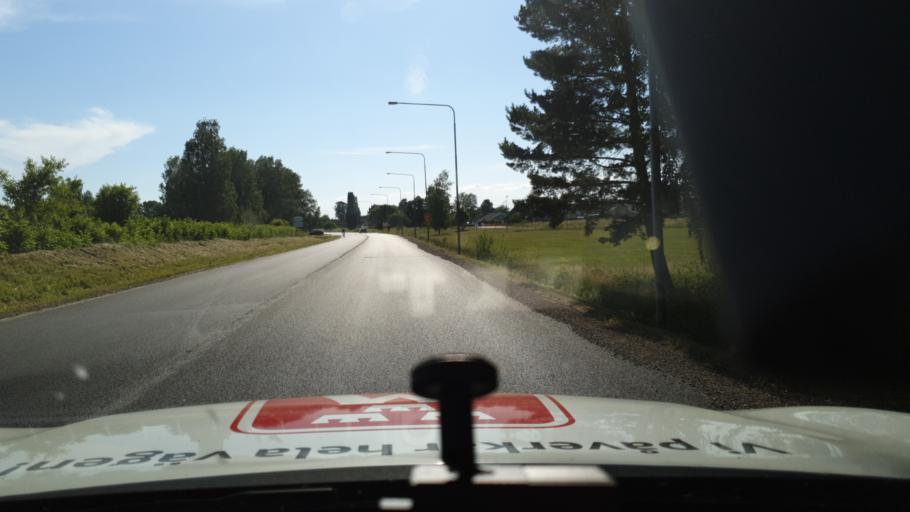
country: SE
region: Vaermland
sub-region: Kils Kommun
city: Kil
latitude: 59.5019
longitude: 13.3028
